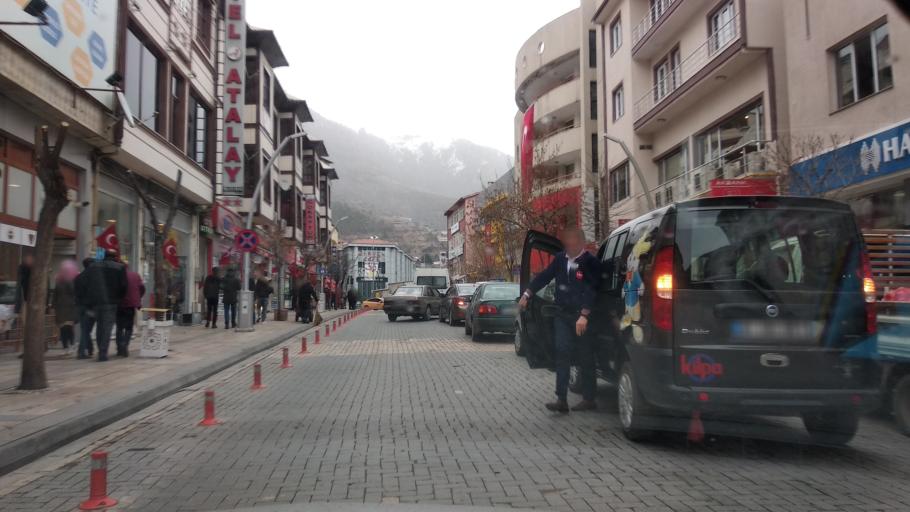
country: TR
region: Gumushane
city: Gumushkhane
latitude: 40.4589
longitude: 39.4810
